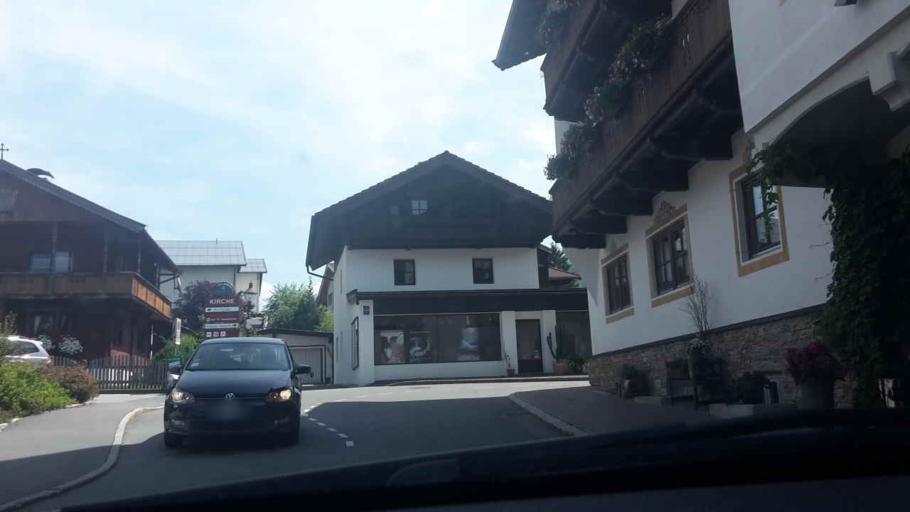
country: AT
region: Tyrol
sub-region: Politischer Bezirk Kitzbuhel
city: Kirchberg in Tirol
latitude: 47.4461
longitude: 12.3156
